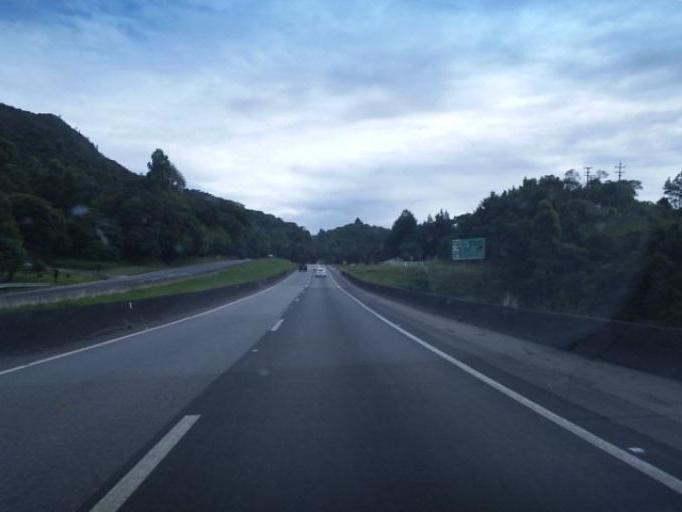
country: BR
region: Parana
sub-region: Campina Grande Do Sul
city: Campina Grande do Sul
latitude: -25.1700
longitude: -48.8672
